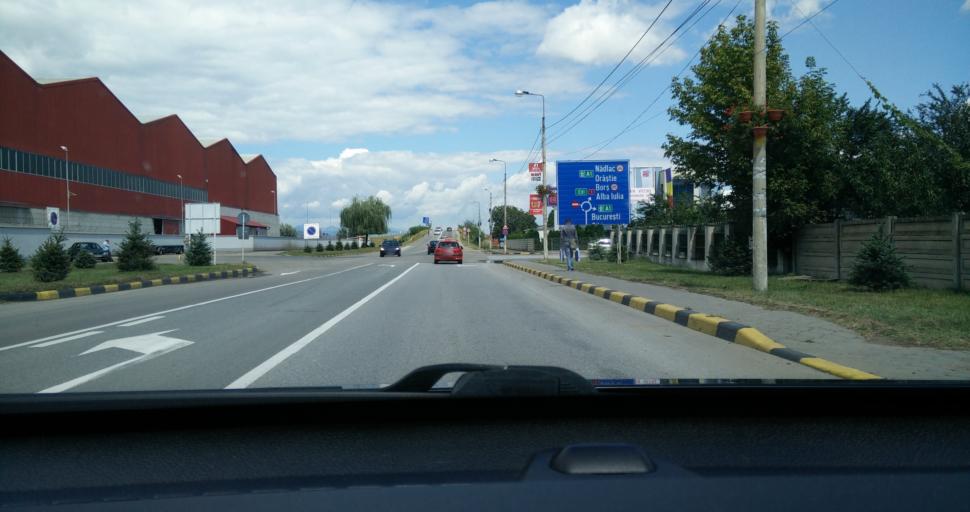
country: RO
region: Alba
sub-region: Municipiul Sebes
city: Lancram
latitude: 45.9693
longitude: 23.5576
